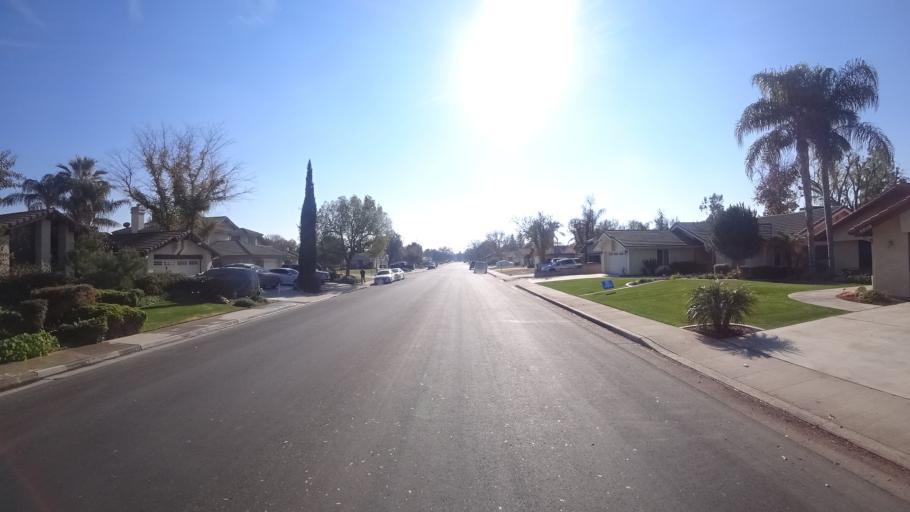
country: US
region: California
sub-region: Kern County
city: Greenacres
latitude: 35.3234
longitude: -119.1135
